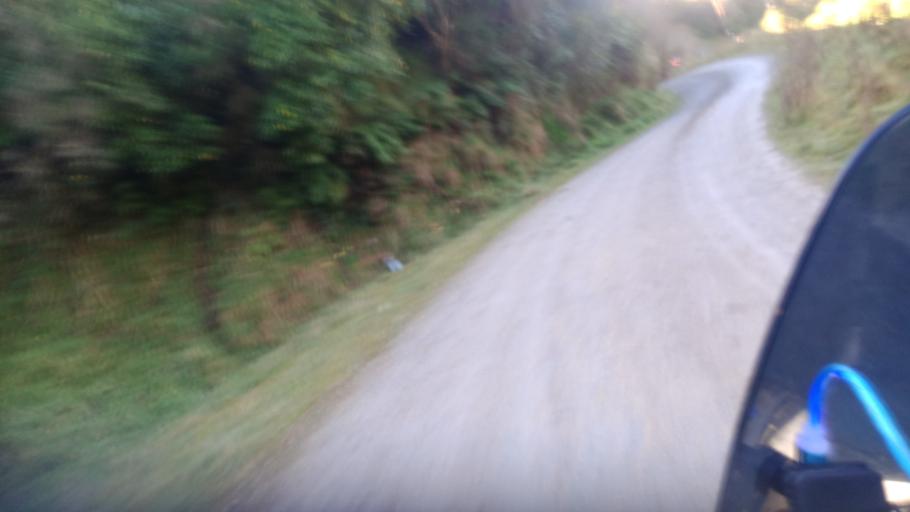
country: NZ
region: Hawke's Bay
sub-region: Wairoa District
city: Wairoa
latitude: -38.6648
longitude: 177.4808
